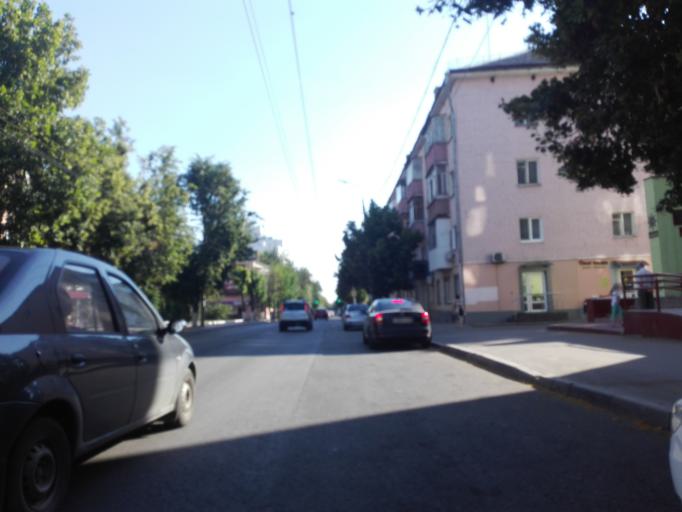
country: RU
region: Orjol
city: Orel
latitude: 52.9745
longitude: 36.0616
